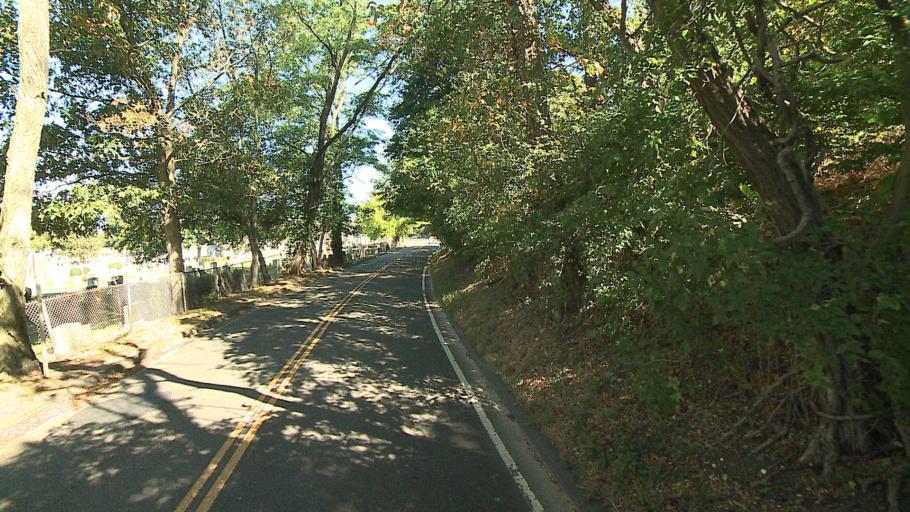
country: US
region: Connecticut
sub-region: Fairfield County
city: Darien
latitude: 41.0899
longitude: -73.5121
